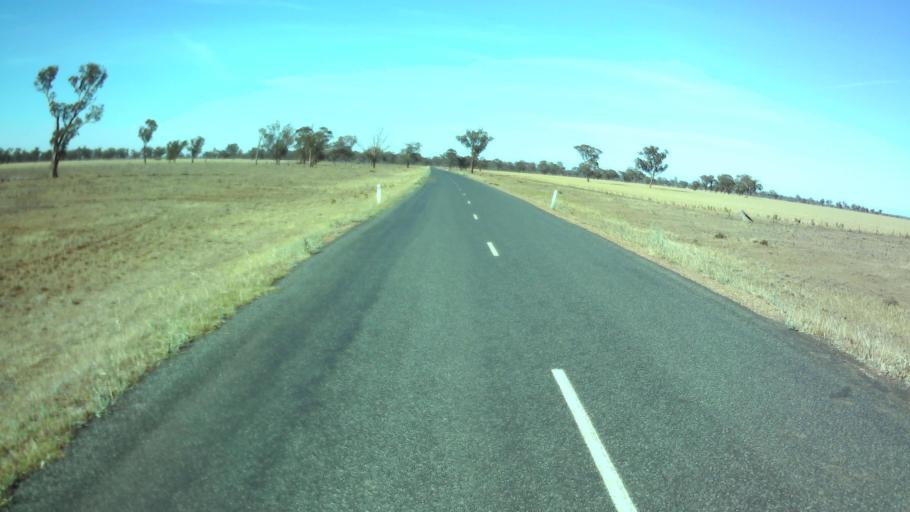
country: AU
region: New South Wales
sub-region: Weddin
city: Grenfell
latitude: -34.0507
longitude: 147.9196
